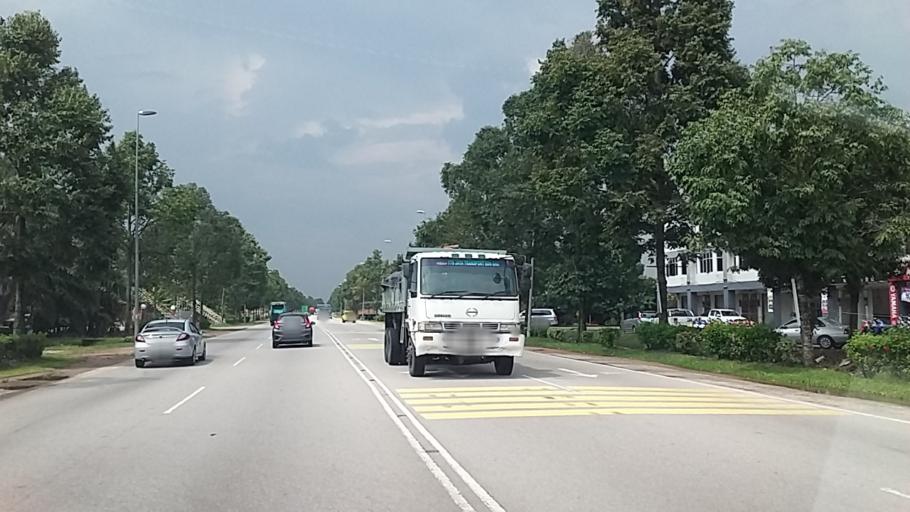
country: MY
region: Johor
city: Parit Raja
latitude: 1.8682
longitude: 103.1210
